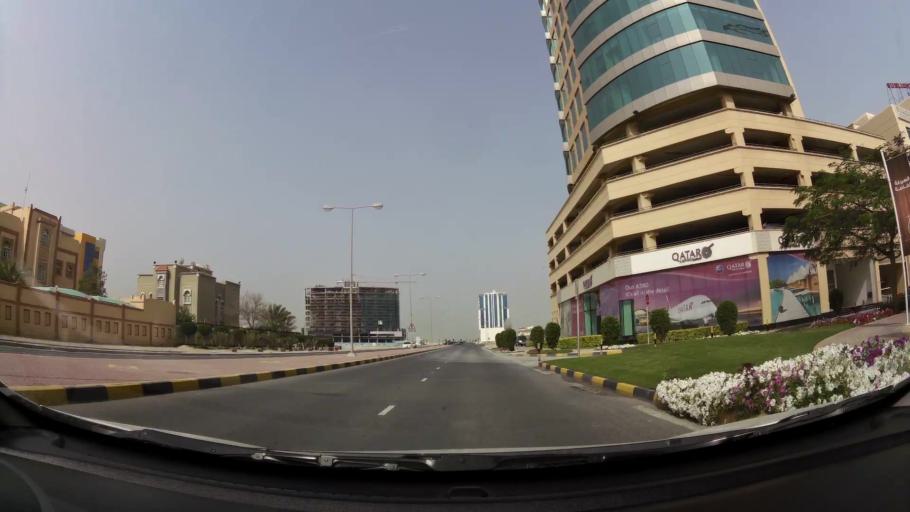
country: BH
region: Manama
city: Jidd Hafs
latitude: 26.2357
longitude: 50.5315
